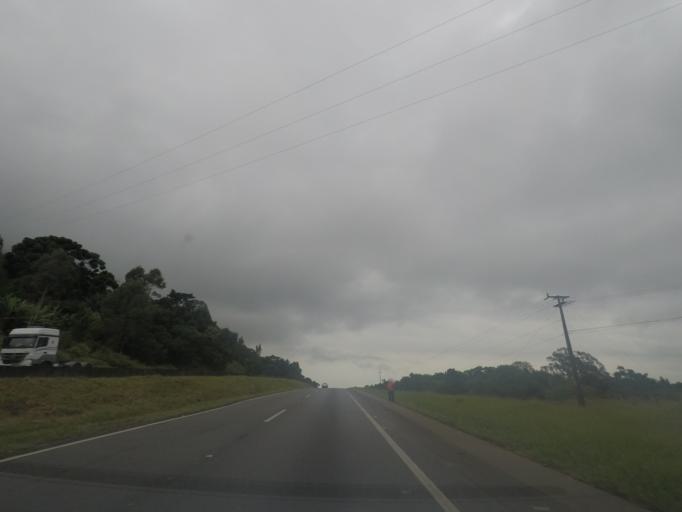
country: BR
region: Parana
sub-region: Campina Grande Do Sul
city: Campina Grande do Sul
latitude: -25.1424
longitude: -48.8568
